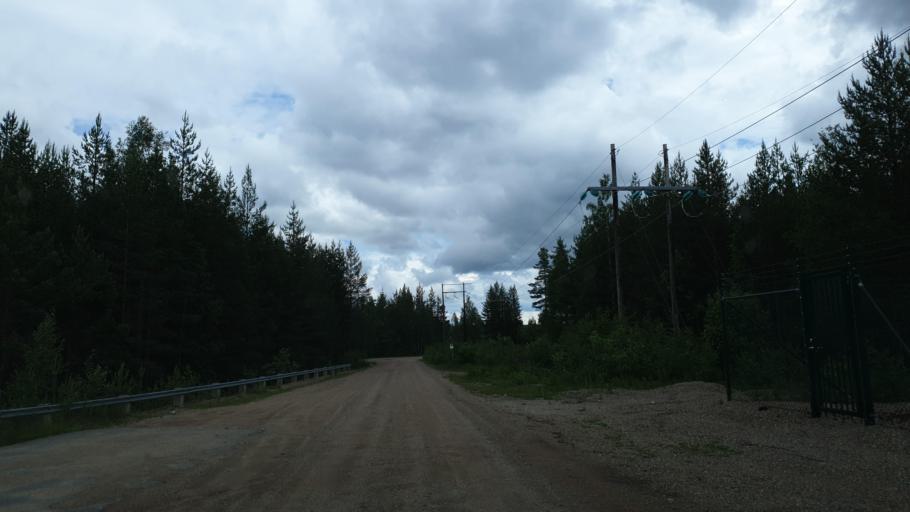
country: SE
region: Jaemtland
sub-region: Harjedalens Kommun
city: Sveg
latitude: 62.0413
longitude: 14.4966
